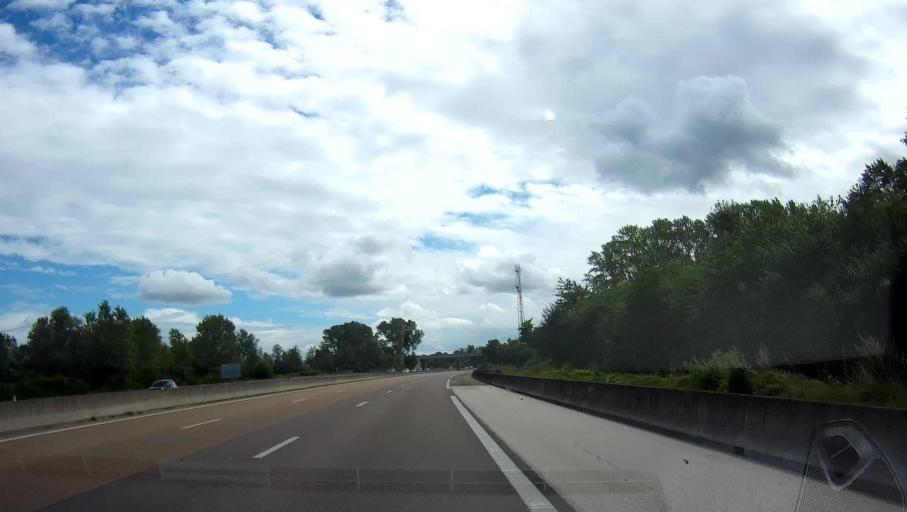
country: FR
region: Bourgogne
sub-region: Departement de la Cote-d'Or
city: Saint-Julien
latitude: 47.4055
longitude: 5.1818
